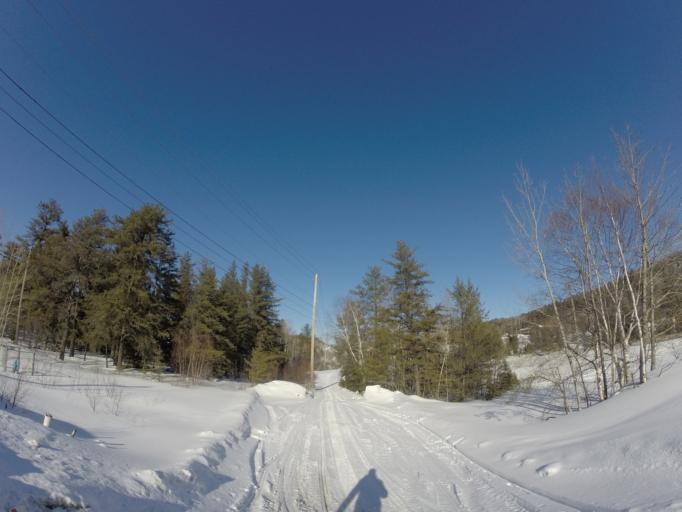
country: CA
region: Ontario
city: Rayside-Balfour
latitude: 46.6355
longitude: -81.3941
